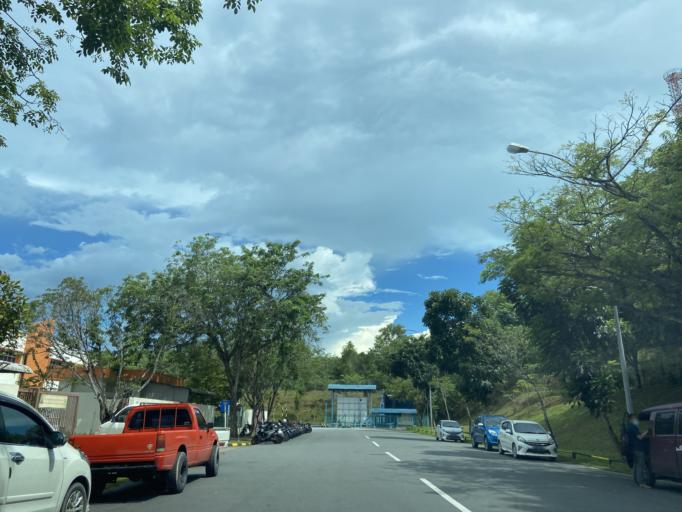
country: SG
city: Singapore
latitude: 1.0562
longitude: 104.0356
